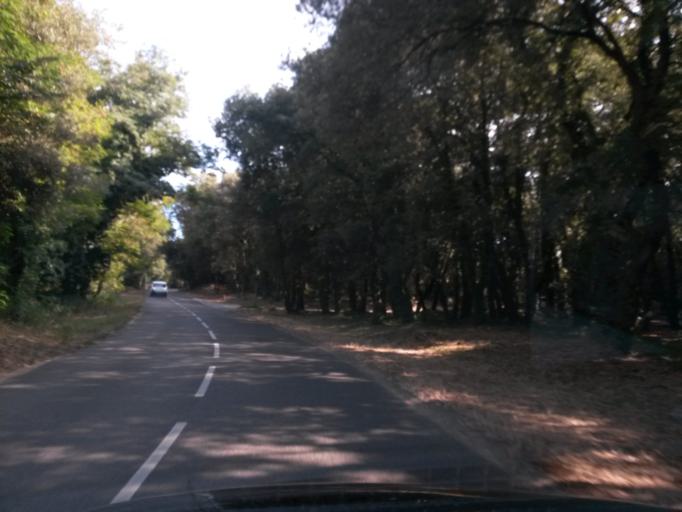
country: FR
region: Pays de la Loire
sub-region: Departement de la Vendee
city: Olonne-sur-Mer
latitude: 46.5296
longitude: -1.8121
